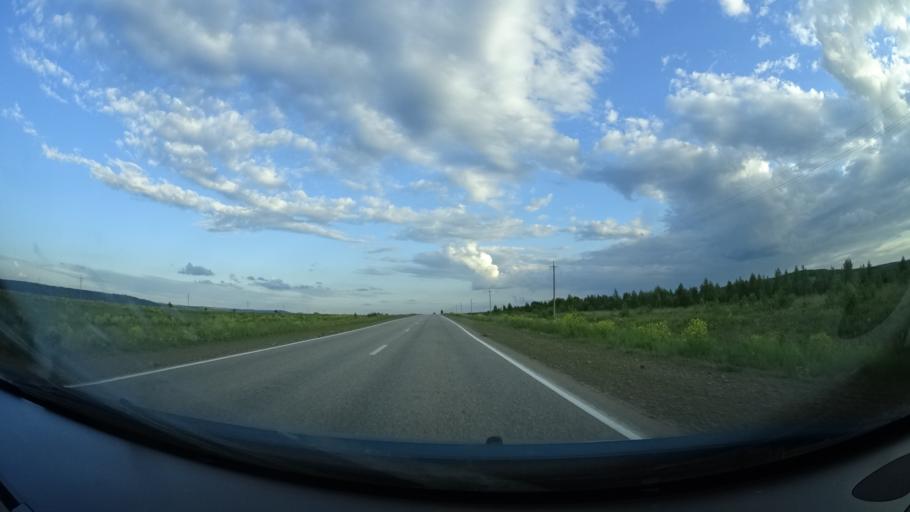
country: RU
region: Perm
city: Barda
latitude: 57.0525
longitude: 55.5439
